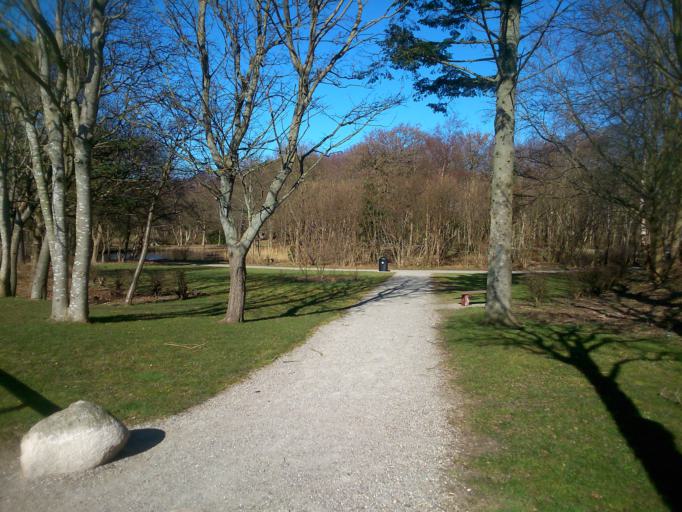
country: DK
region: Central Jutland
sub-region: Ringkobing-Skjern Kommune
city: Ringkobing
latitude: 56.0844
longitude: 8.2614
